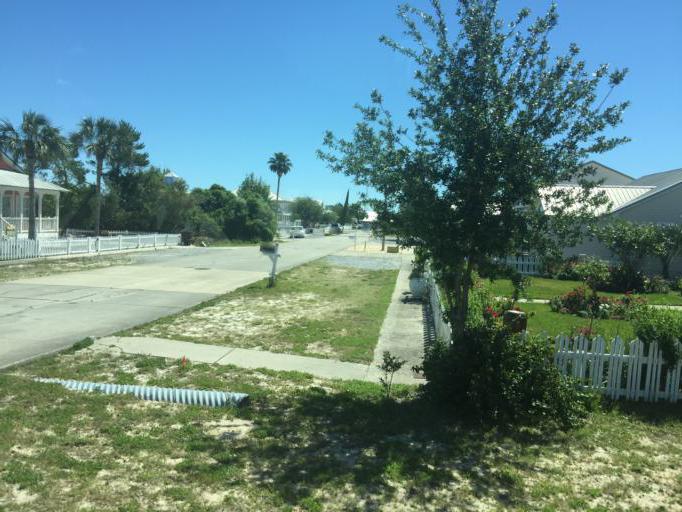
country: US
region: Florida
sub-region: Bay County
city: Panama City Beach
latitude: 30.2066
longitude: -85.8477
